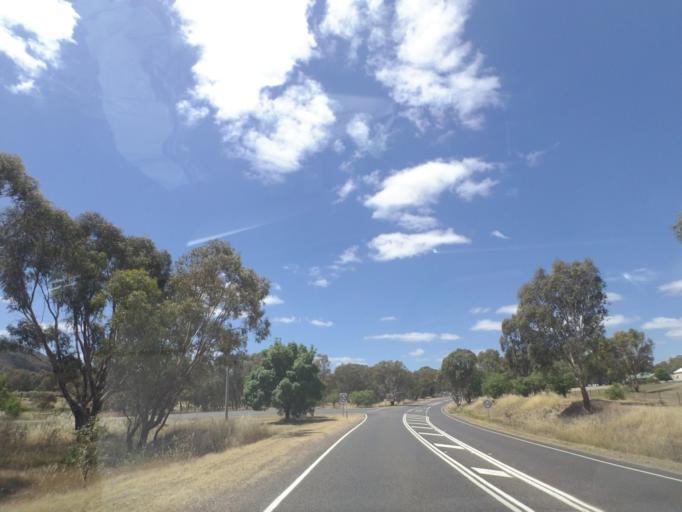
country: AU
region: Victoria
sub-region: Wangaratta
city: Wangaratta
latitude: -36.4646
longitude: 146.2157
